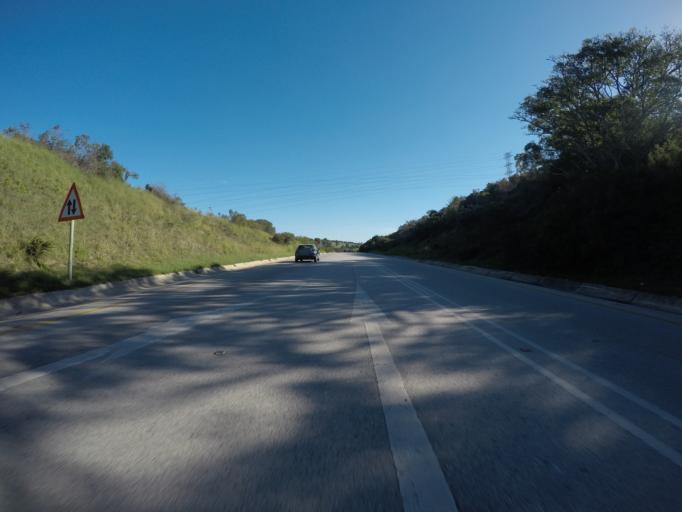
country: ZA
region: Eastern Cape
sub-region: Cacadu District Municipality
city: Jeffrey's Bay
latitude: -33.9084
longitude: 25.0727
